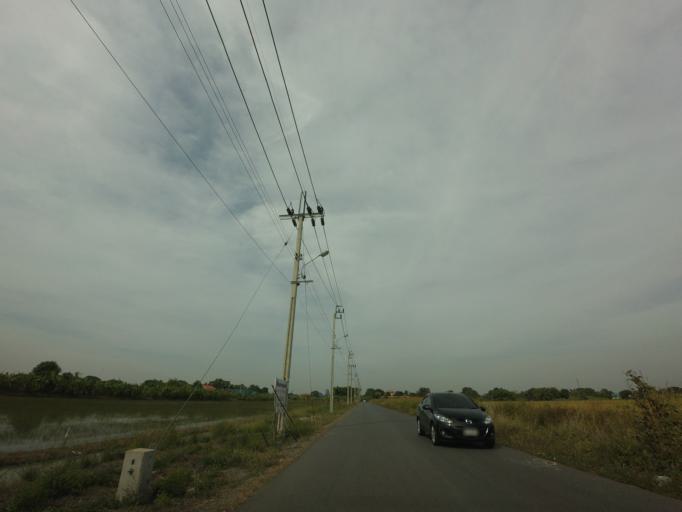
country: TH
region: Bangkok
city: Khlong Sam Wa
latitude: 13.8885
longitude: 100.7039
